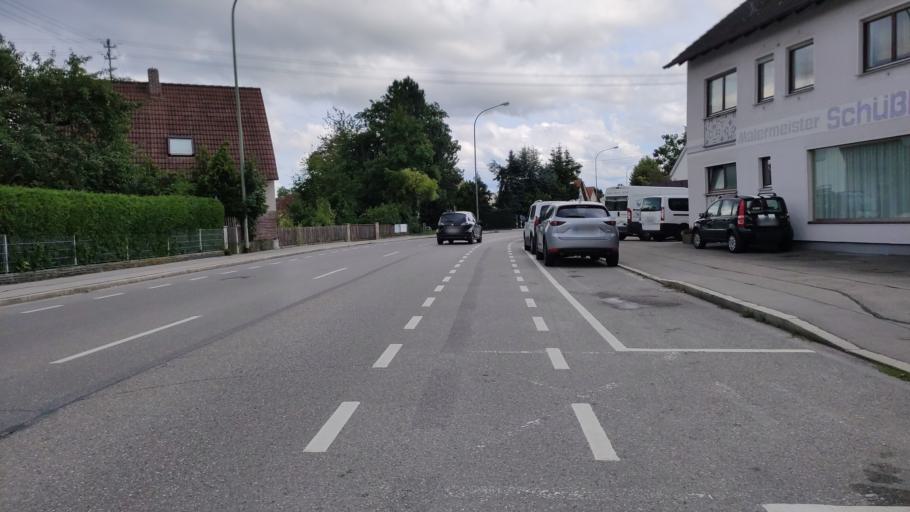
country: DE
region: Bavaria
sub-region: Swabia
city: Konigsbrunn
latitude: 48.2636
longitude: 10.8874
